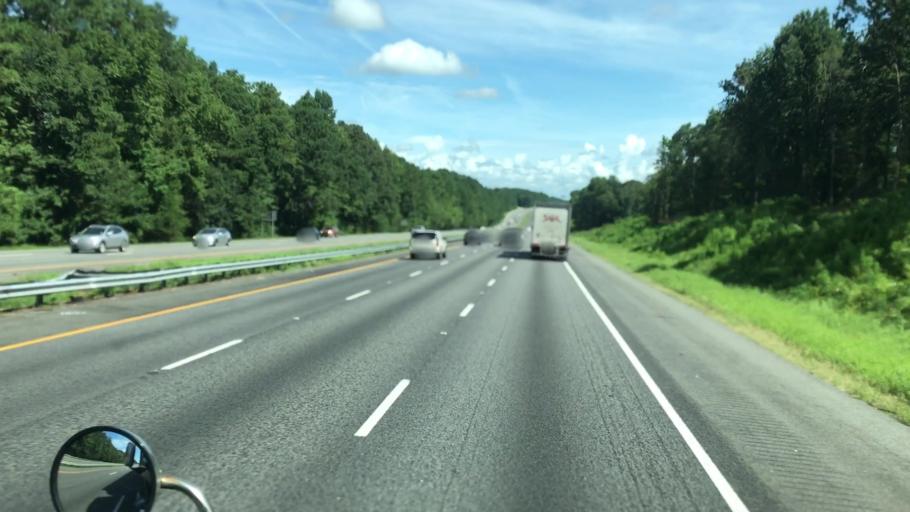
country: US
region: Georgia
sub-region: Monroe County
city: Forsyth
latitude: 33.0984
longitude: -83.9992
